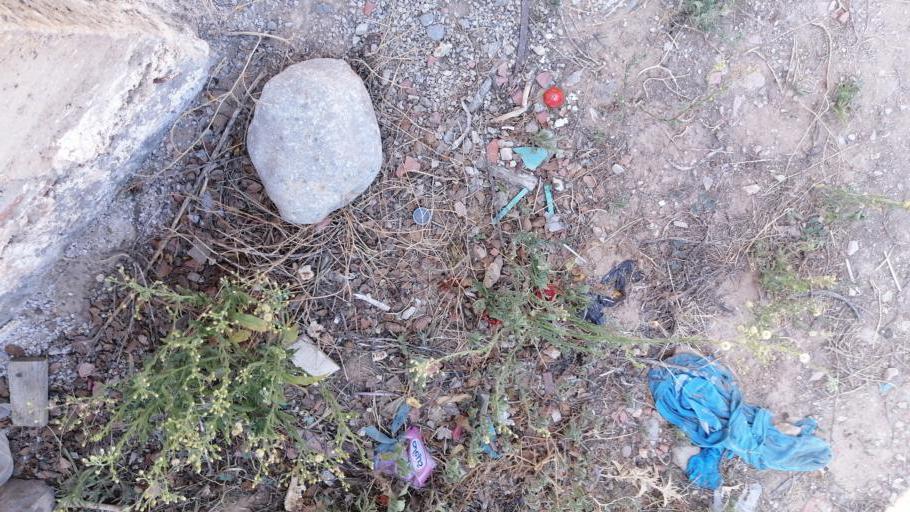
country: TN
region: Al Qayrawan
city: Sbikha
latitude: 36.1184
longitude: 10.0980
